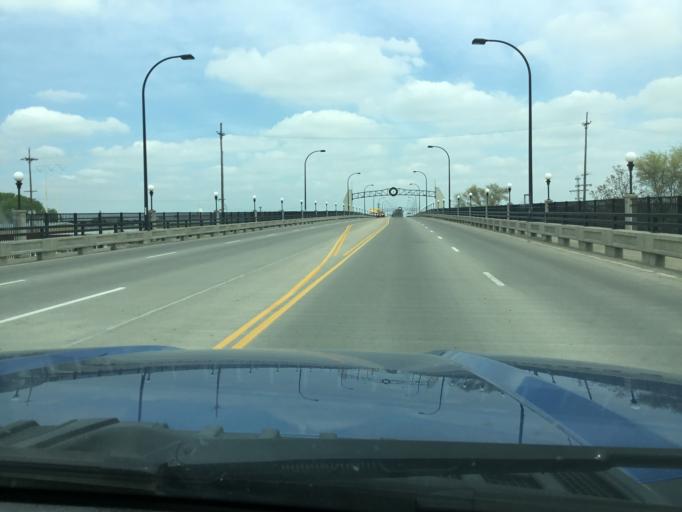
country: US
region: Kansas
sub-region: Shawnee County
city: Topeka
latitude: 39.0608
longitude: -95.6757
